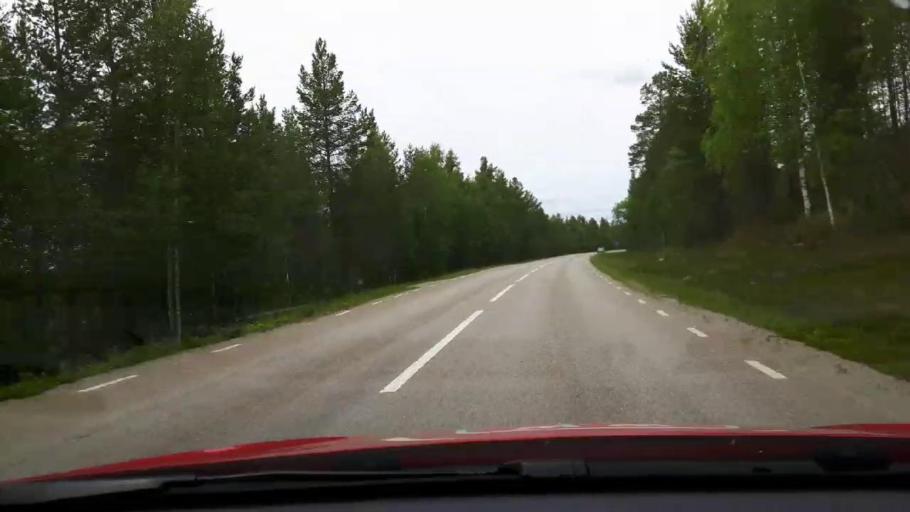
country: SE
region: Jaemtland
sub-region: Harjedalens Kommun
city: Sveg
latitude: 62.2440
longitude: 13.8451
